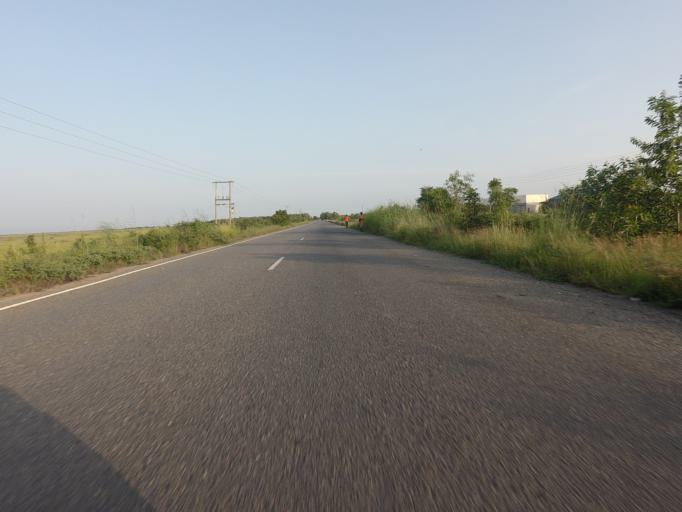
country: GH
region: Volta
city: Anloga
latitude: 5.9026
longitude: 0.7123
